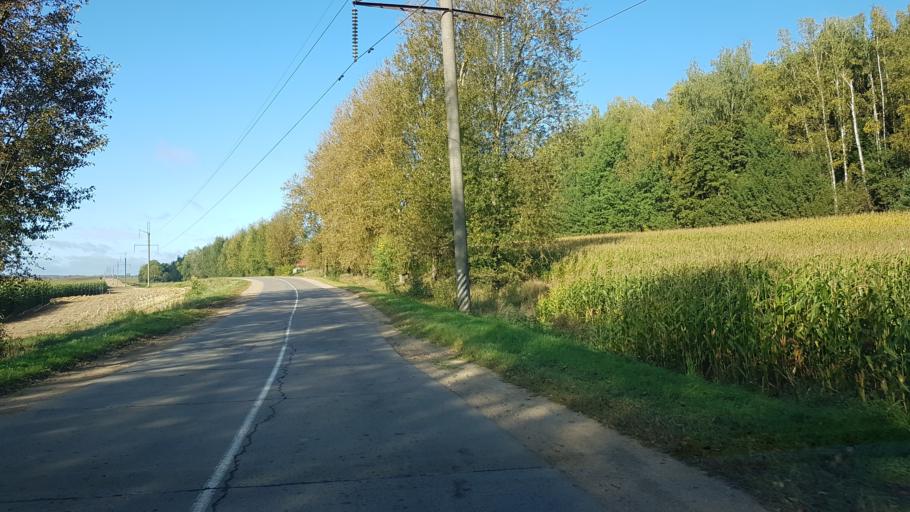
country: BY
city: Fanipol
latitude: 53.7364
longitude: 27.2369
